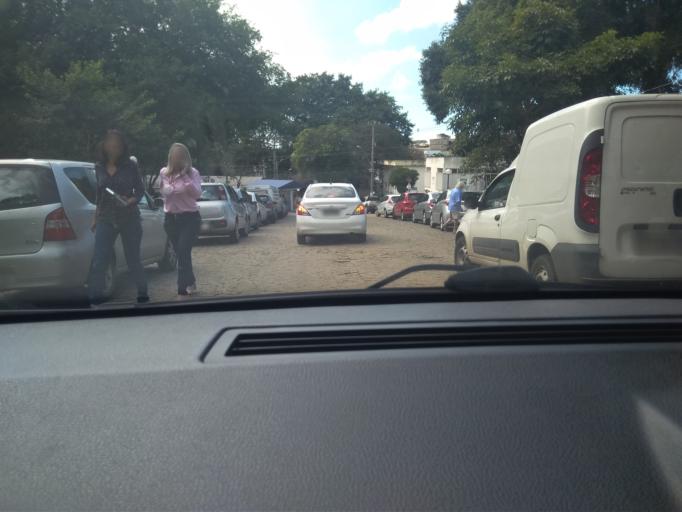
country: BR
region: Espirito Santo
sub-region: Vitoria
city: Vitoria
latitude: -20.2996
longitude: -40.3177
